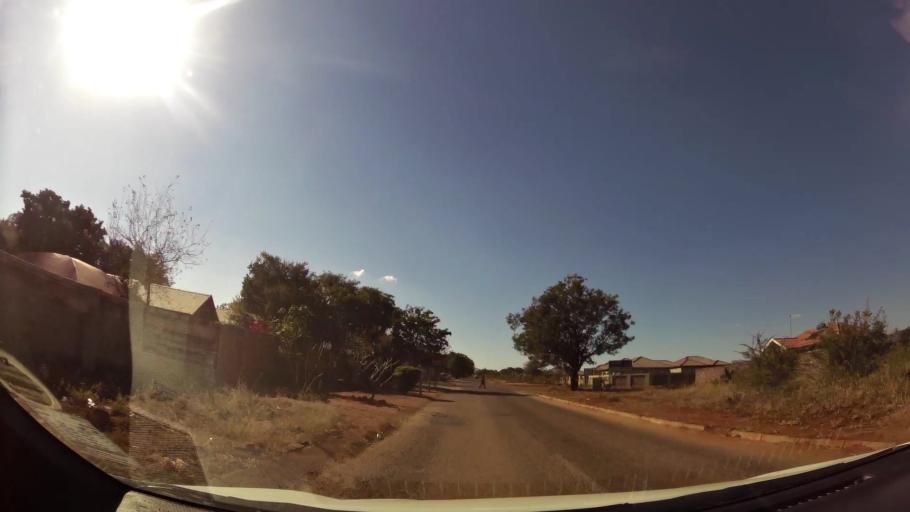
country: ZA
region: Limpopo
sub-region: Waterberg District Municipality
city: Mokopane
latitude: -24.1970
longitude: 28.9945
